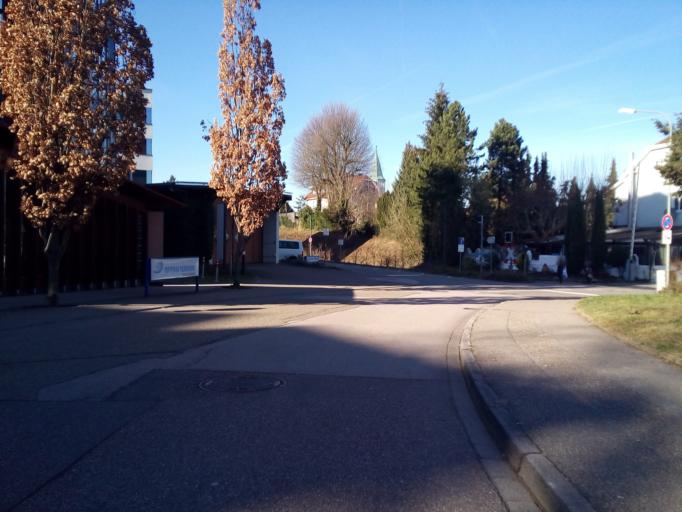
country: DE
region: Baden-Wuerttemberg
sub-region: Freiburg Region
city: Achern
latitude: 48.6252
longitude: 8.0679
